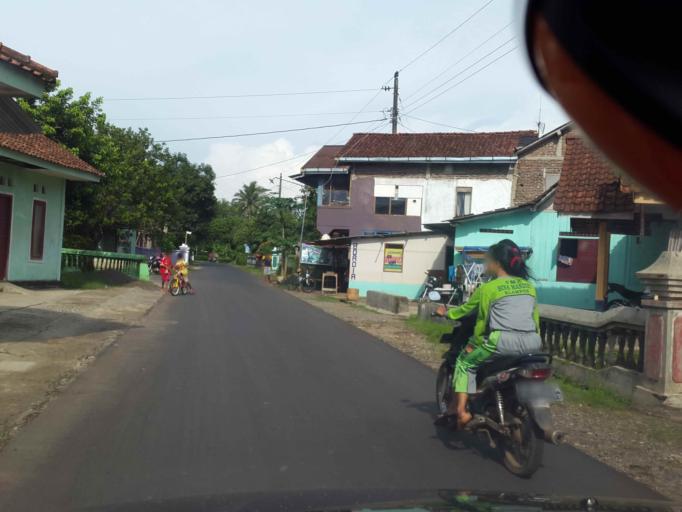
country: ID
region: Central Java
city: Purbalingga
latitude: -7.4610
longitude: 109.4890
